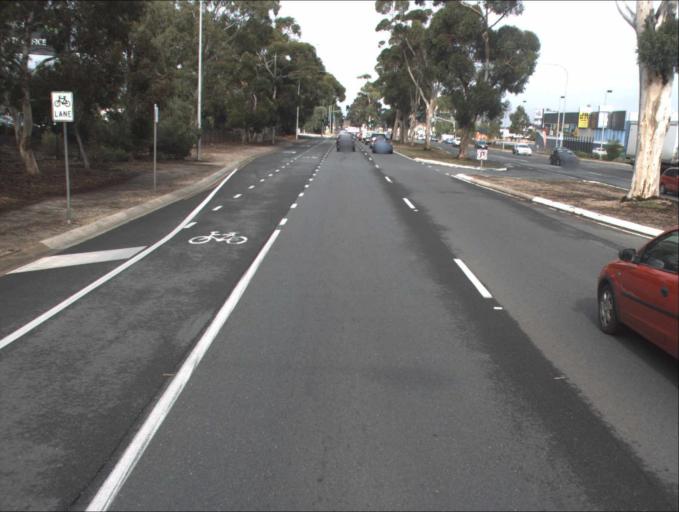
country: AU
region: South Australia
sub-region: Port Adelaide Enfield
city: Enfield
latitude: -34.8378
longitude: 138.6079
